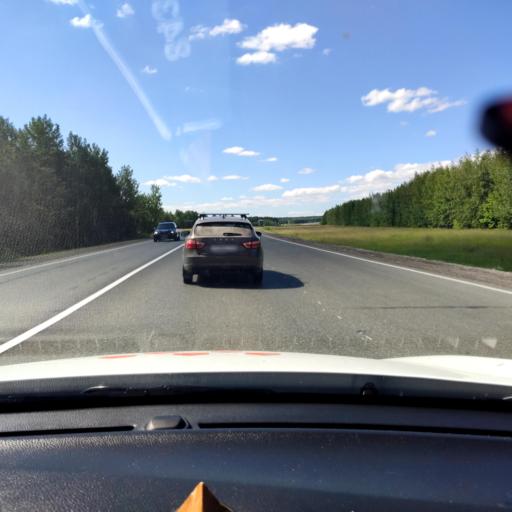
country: RU
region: Tatarstan
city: Verkhniy Uslon
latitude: 55.6743
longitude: 48.8696
